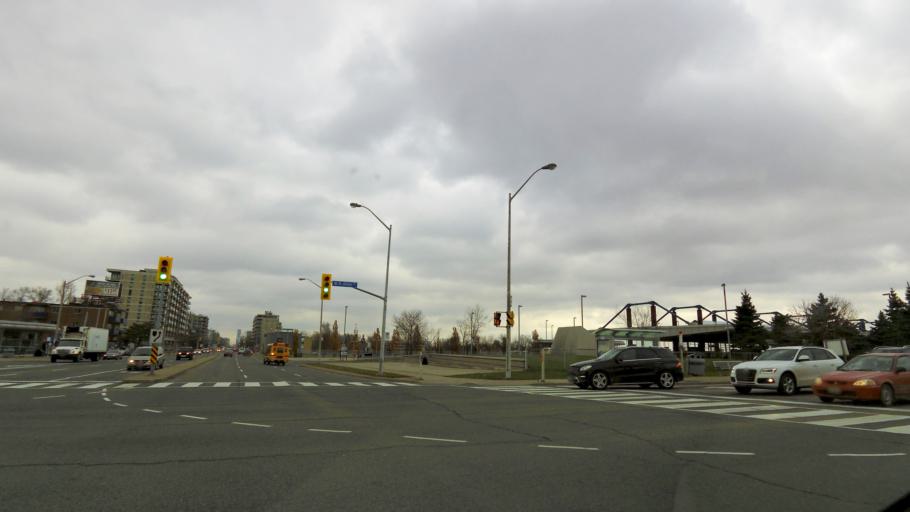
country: CA
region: Ontario
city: North York
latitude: 43.7502
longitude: -79.4635
